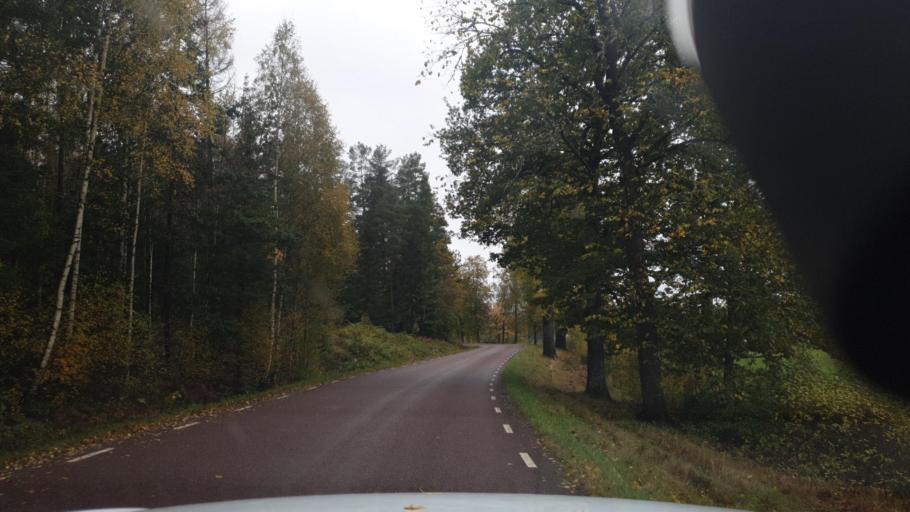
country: SE
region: Vaermland
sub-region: Karlstads Kommun
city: Valberg
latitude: 59.4381
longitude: 13.0885
